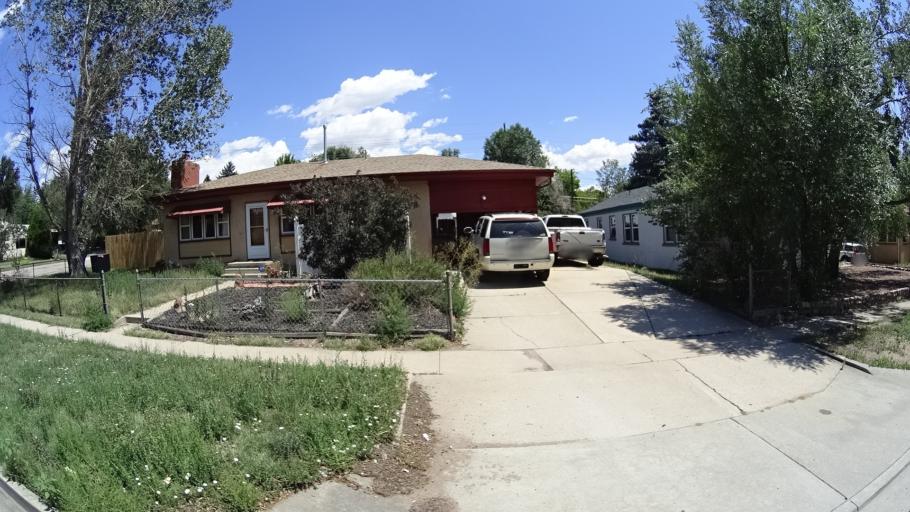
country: US
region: Colorado
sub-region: El Paso County
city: Colorado Springs
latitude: 38.8459
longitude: -104.7942
